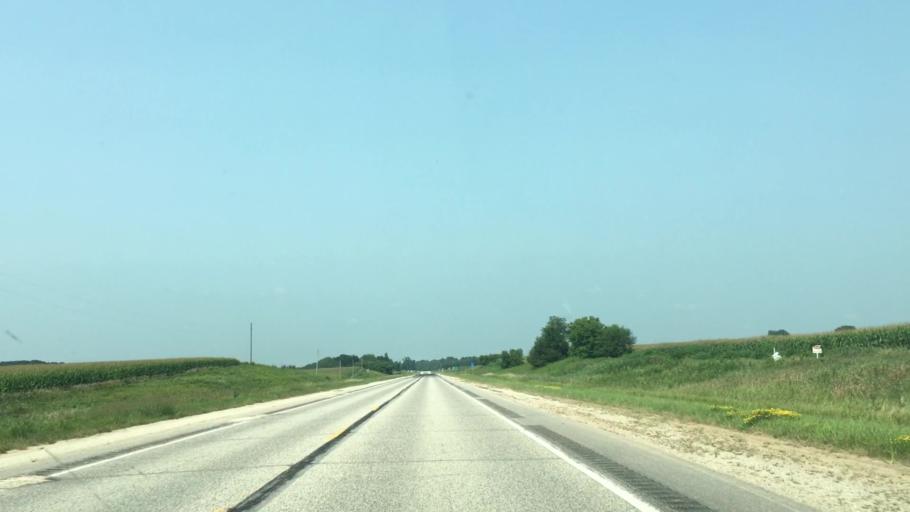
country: US
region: Iowa
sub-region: Fayette County
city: Fayette
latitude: 42.8128
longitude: -91.8051
